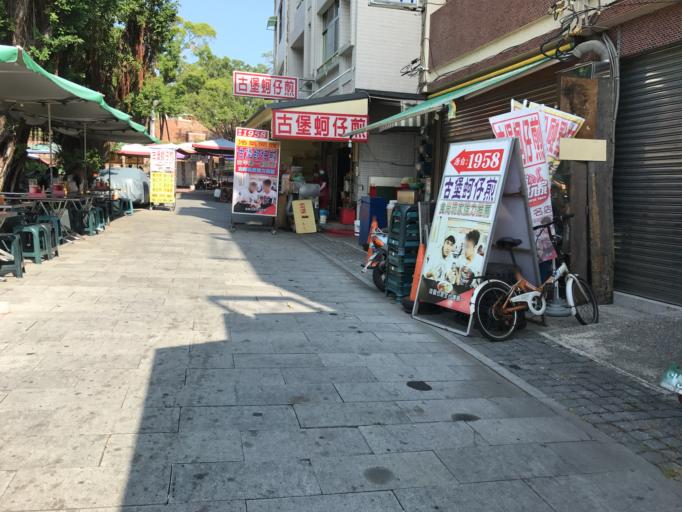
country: TW
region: Taiwan
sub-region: Tainan
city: Tainan
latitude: 23.0007
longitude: 120.1612
